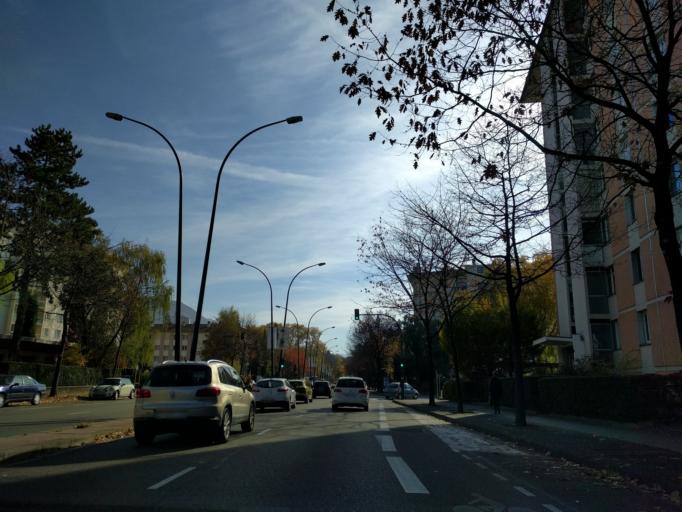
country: FR
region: Rhone-Alpes
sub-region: Departement de la Haute-Savoie
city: Annecy-le-Vieux
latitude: 45.9076
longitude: 6.1403
